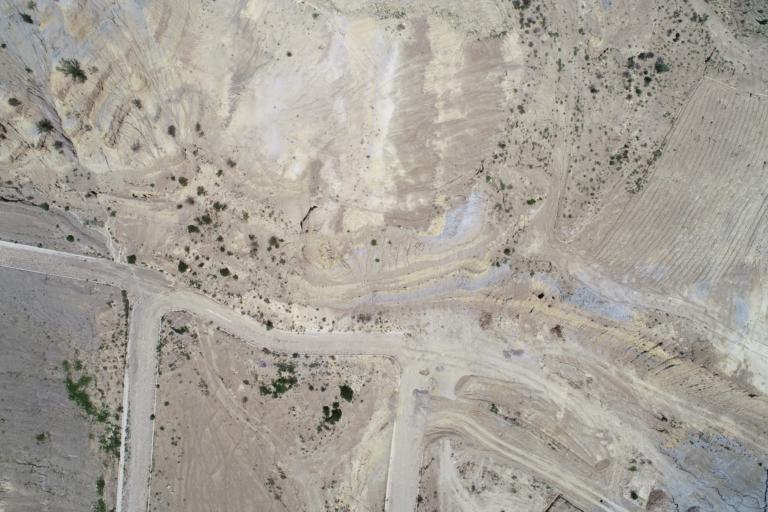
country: BO
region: La Paz
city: La Paz
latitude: -16.5240
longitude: -68.0479
